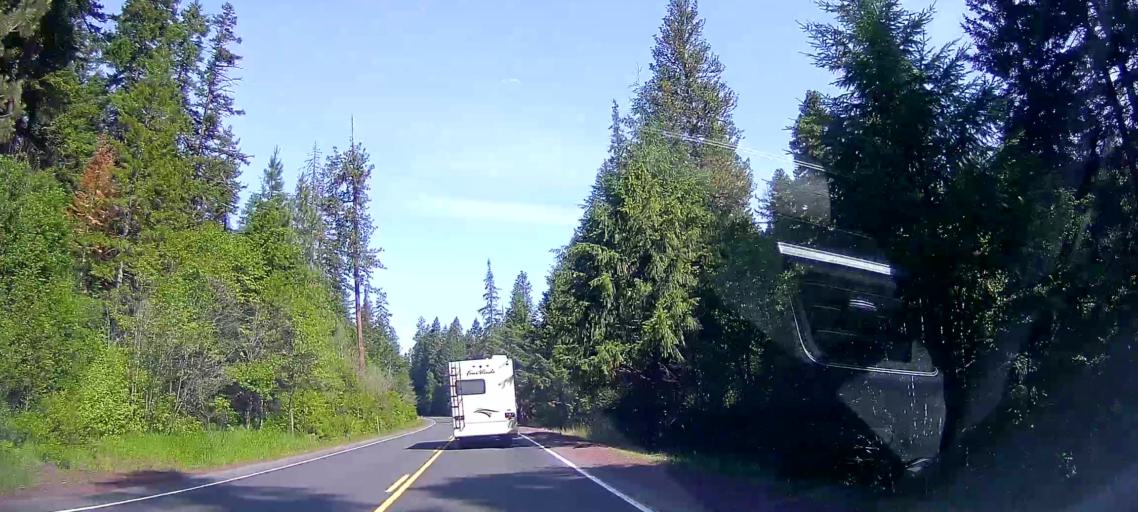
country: US
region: Oregon
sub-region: Jefferson County
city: Warm Springs
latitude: 45.0694
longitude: -121.5267
